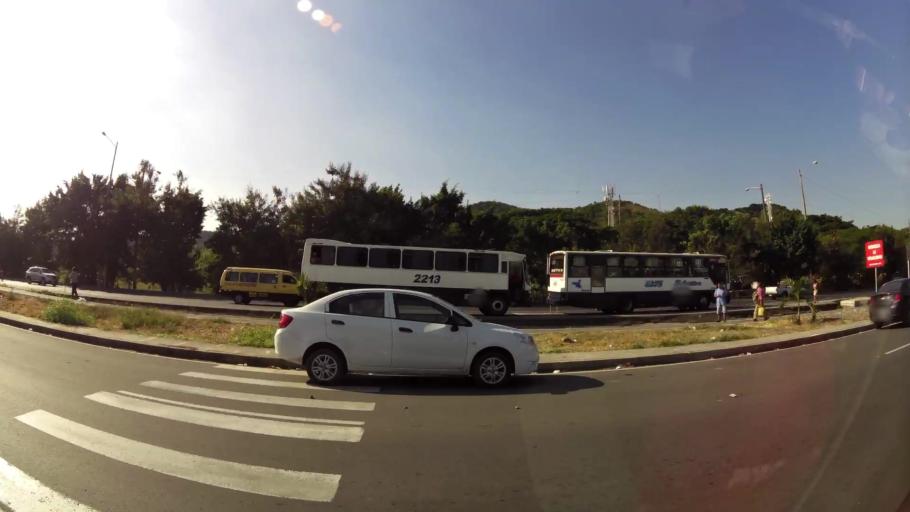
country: EC
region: Guayas
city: Santa Lucia
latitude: -2.1866
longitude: -79.9651
